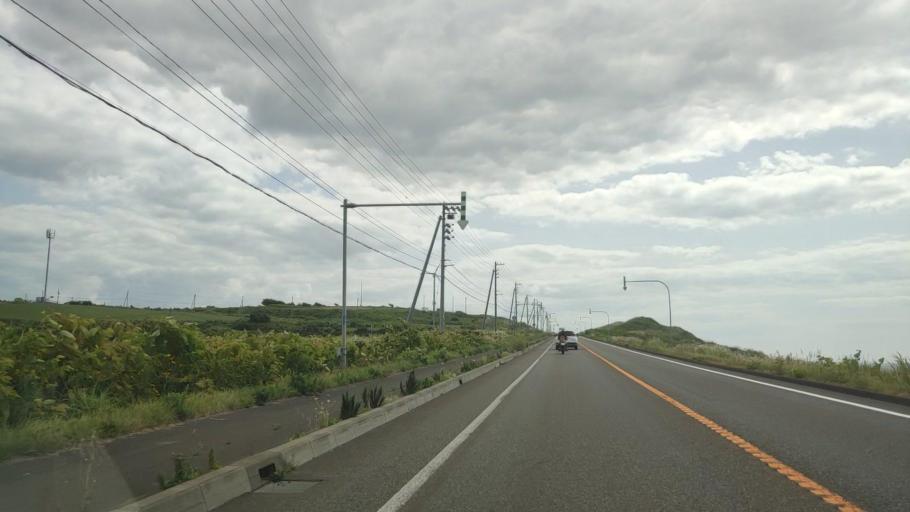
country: JP
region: Hokkaido
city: Rumoi
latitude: 44.5243
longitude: 141.7655
